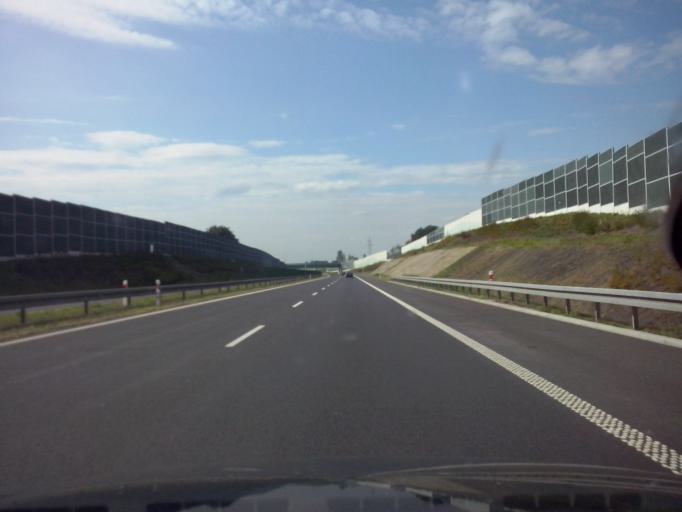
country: PL
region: Lesser Poland Voivodeship
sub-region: Powiat tarnowski
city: Lukowa
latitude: 50.0597
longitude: 20.9930
